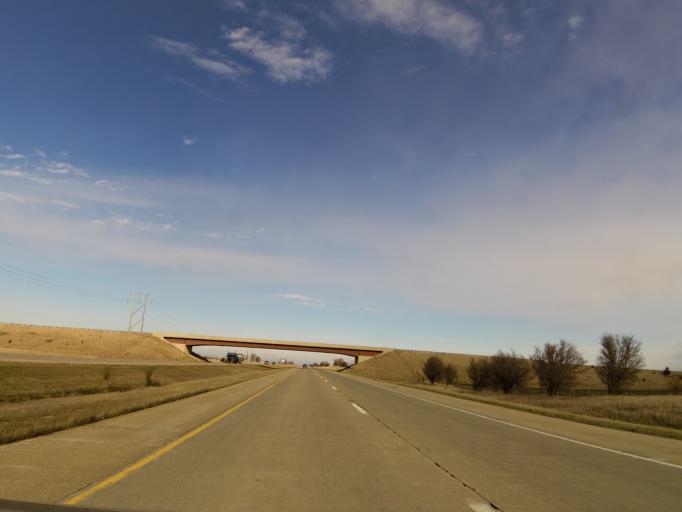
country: US
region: Illinois
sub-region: Marshall County
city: Wenona
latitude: 41.1467
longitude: -89.0755
